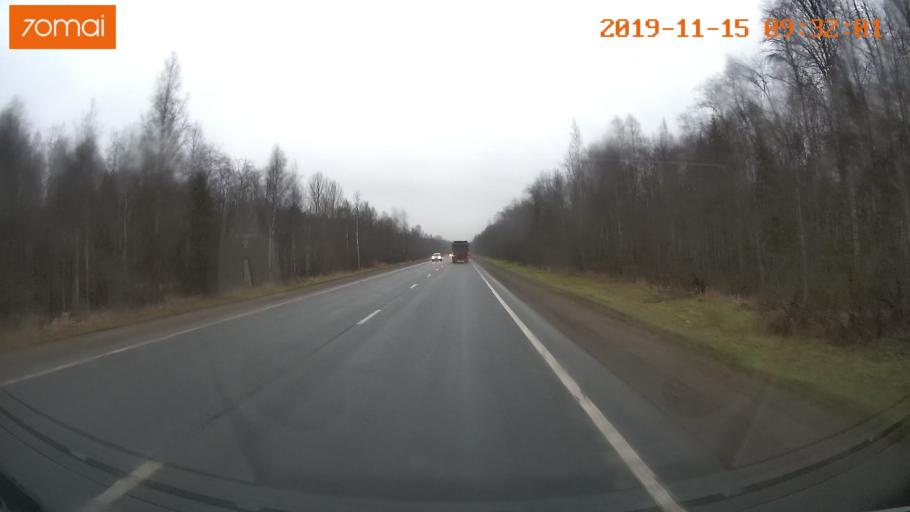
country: RU
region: Vologda
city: Sheksna
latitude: 59.2732
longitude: 38.3245
